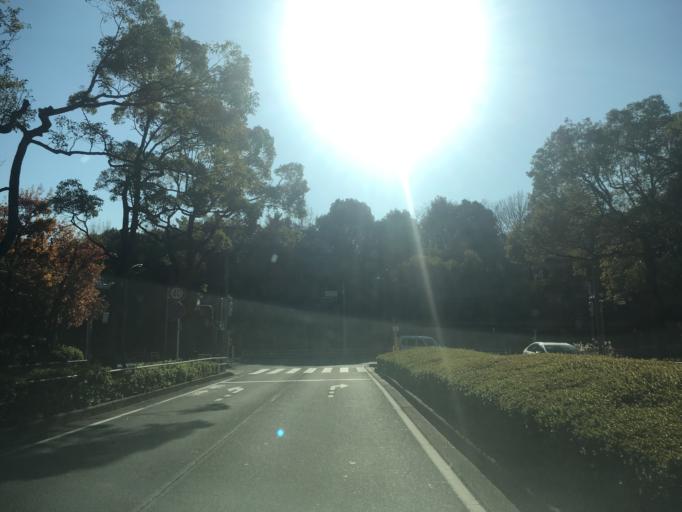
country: JP
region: Tokyo
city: Hino
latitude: 35.6231
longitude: 139.4271
